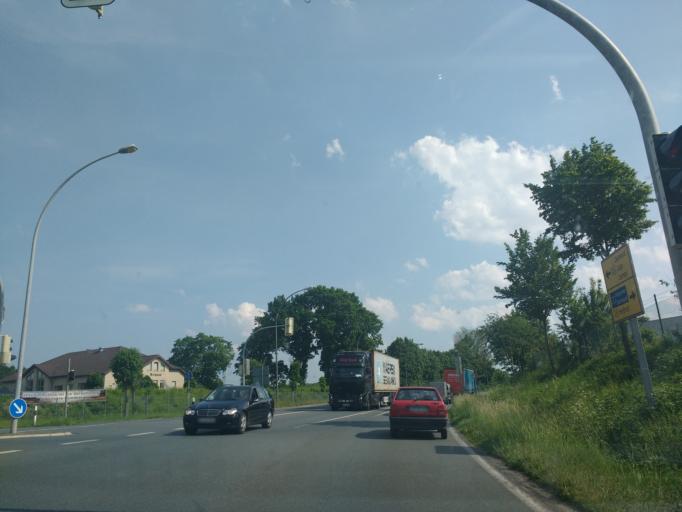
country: DE
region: North Rhine-Westphalia
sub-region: Regierungsbezirk Detmold
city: Bad Salzuflen
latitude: 52.0555
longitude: 8.7590
